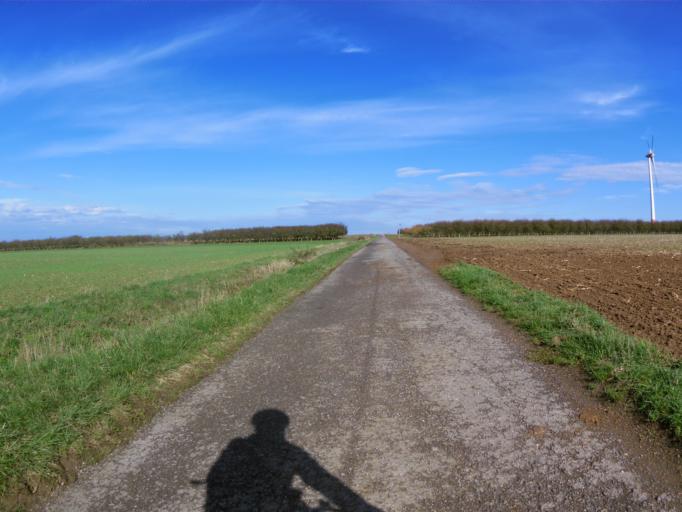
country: DE
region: Bavaria
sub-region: Regierungsbezirk Unterfranken
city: Sommerhausen
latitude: 49.7144
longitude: 10.0389
